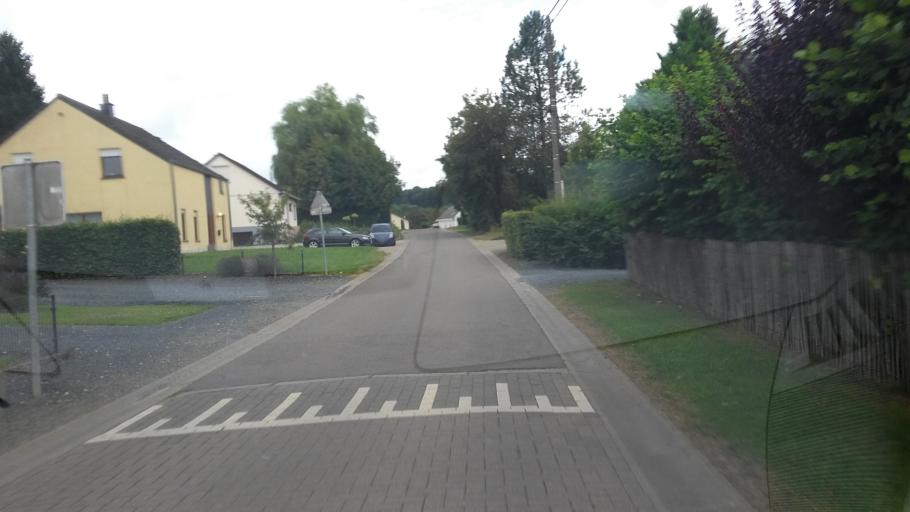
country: BE
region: Wallonia
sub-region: Province du Luxembourg
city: Arlon
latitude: 49.6791
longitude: 5.8429
